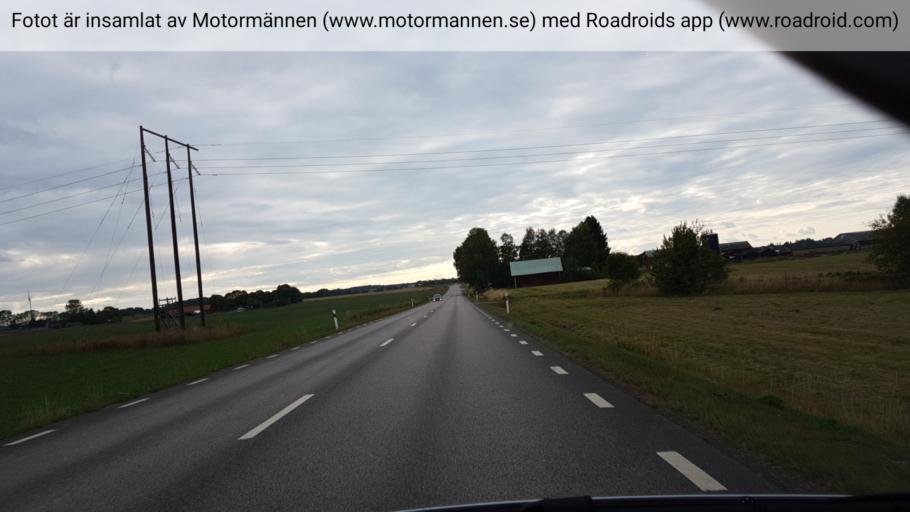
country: SE
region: Vaestra Goetaland
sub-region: Tibro Kommun
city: Tibro
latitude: 58.3485
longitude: 14.1052
